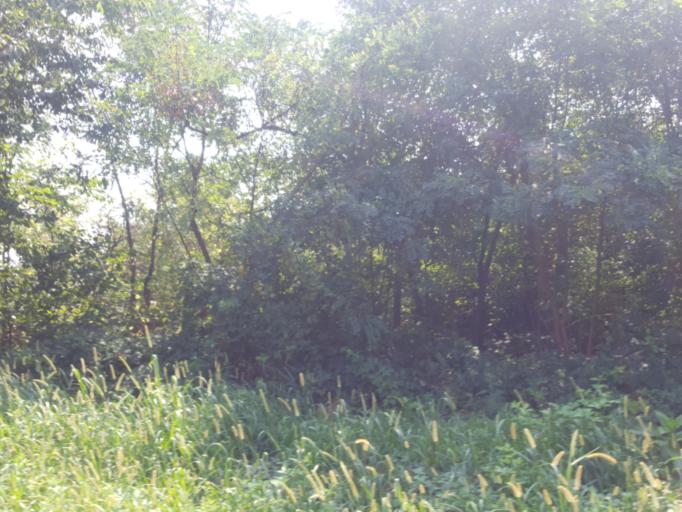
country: IT
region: Lombardy
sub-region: Citta metropolitana di Milano
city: Torrazza dei Mandelli
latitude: 45.5751
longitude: 9.4044
